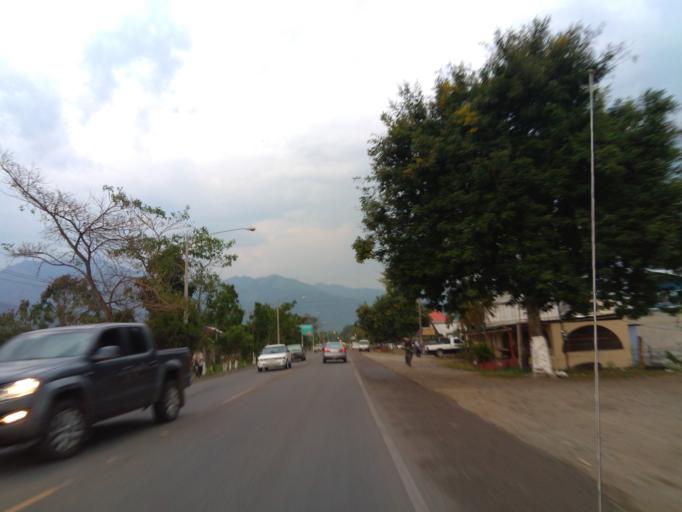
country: HN
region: Yoro
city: El Progreso
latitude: 15.3855
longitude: -87.8052
